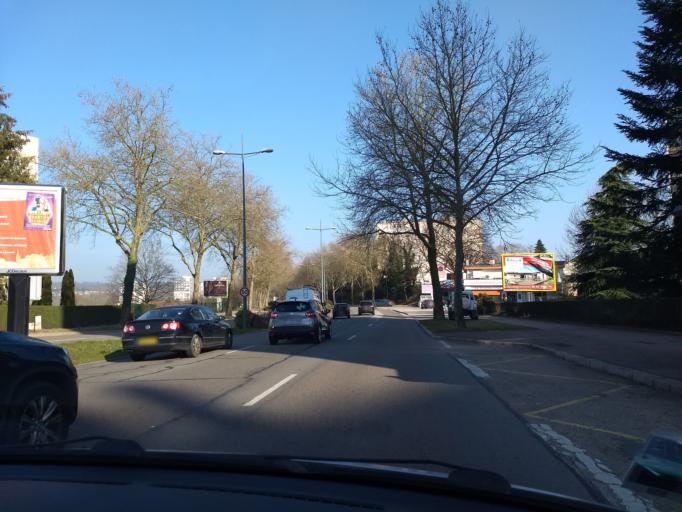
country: FR
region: Limousin
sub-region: Departement de la Haute-Vienne
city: Isle
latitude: 45.8279
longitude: 1.2268
